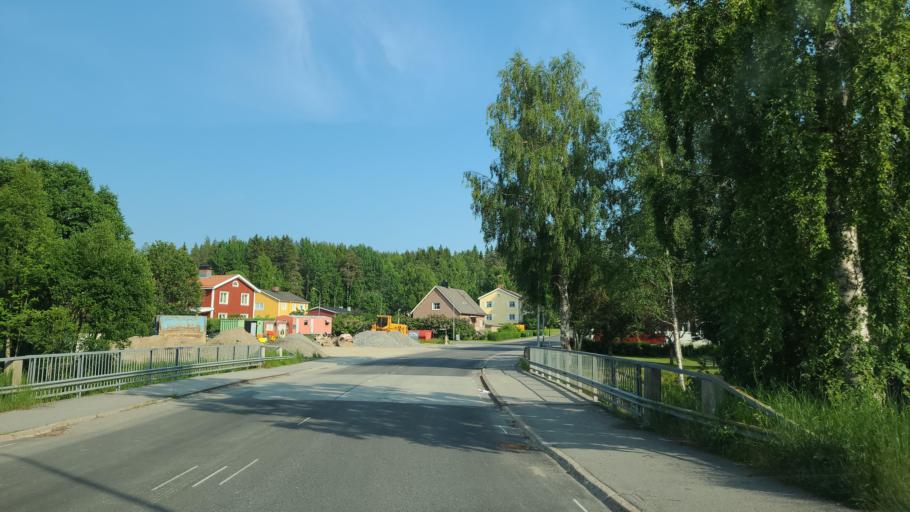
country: SE
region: Vaesterbotten
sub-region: Skelleftea Kommun
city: Burea
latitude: 64.3685
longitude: 21.3203
